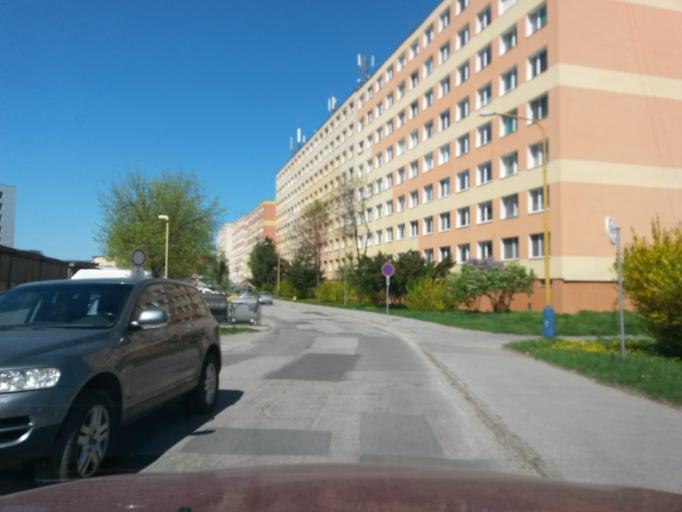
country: SK
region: Kosicky
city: Kosice
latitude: 48.7060
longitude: 21.2499
